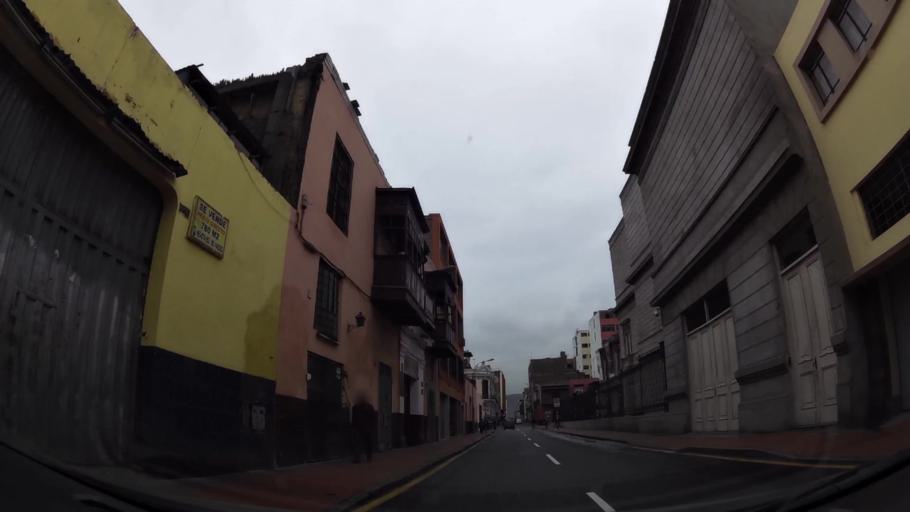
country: PE
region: Lima
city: Lima
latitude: -12.0458
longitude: -77.0356
